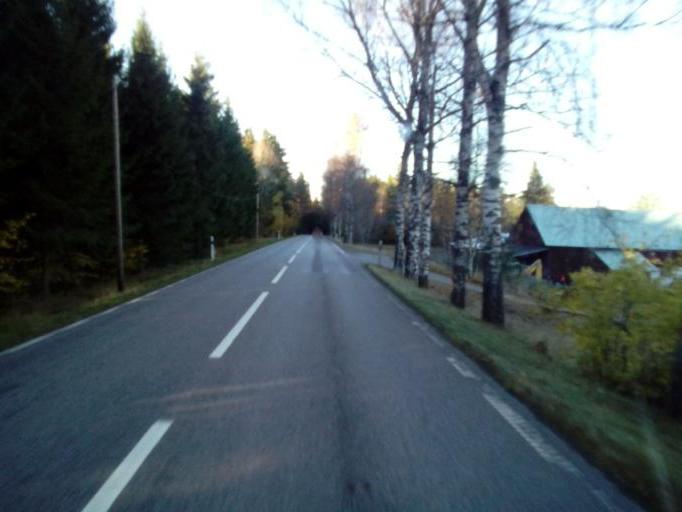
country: SE
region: OErebro
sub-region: Hallsbergs Kommun
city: Palsboda
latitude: 58.8154
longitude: 15.4142
